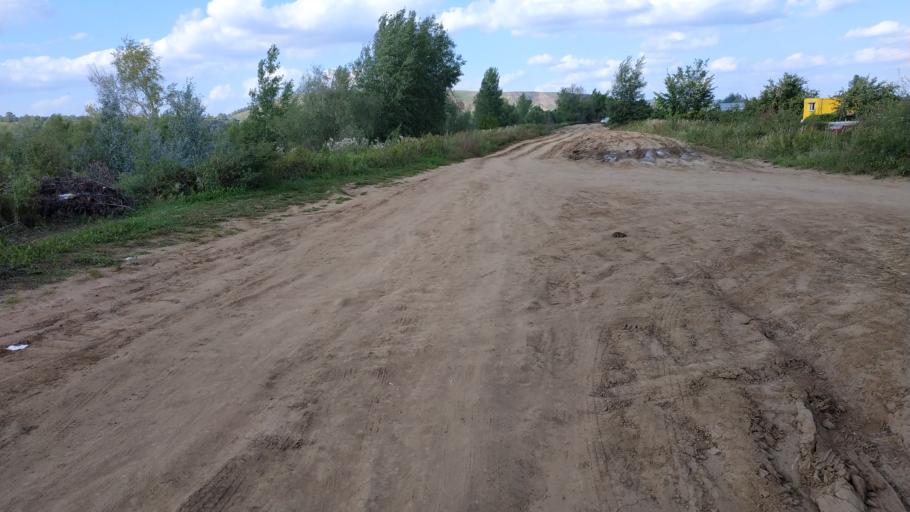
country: RU
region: Tatarstan
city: Nizhnekamsk
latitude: 55.6845
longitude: 51.7316
